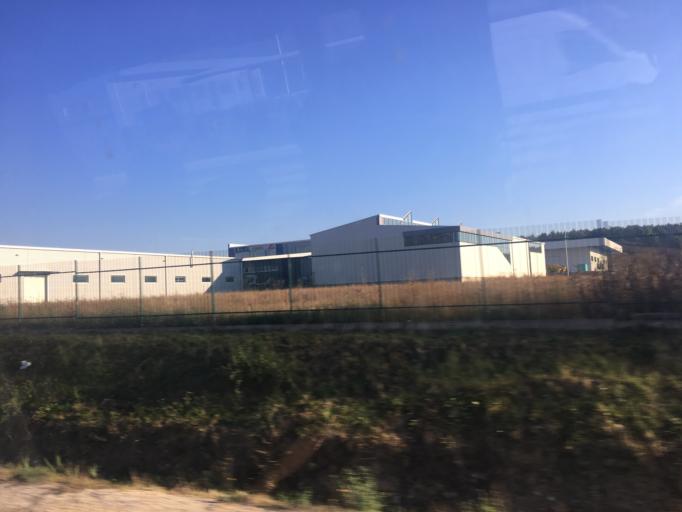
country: XK
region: Pristina
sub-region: Komuna e Drenasit
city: Glogovac
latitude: 42.5997
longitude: 20.9638
